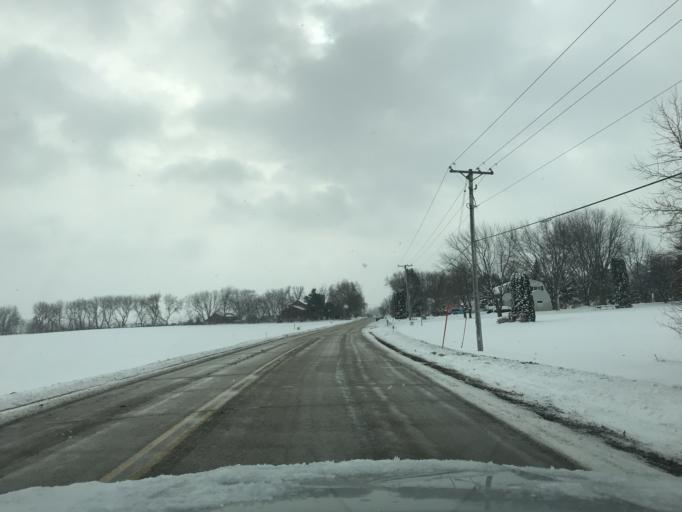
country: US
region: Wisconsin
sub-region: Dane County
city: Windsor
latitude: 43.1714
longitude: -89.2857
